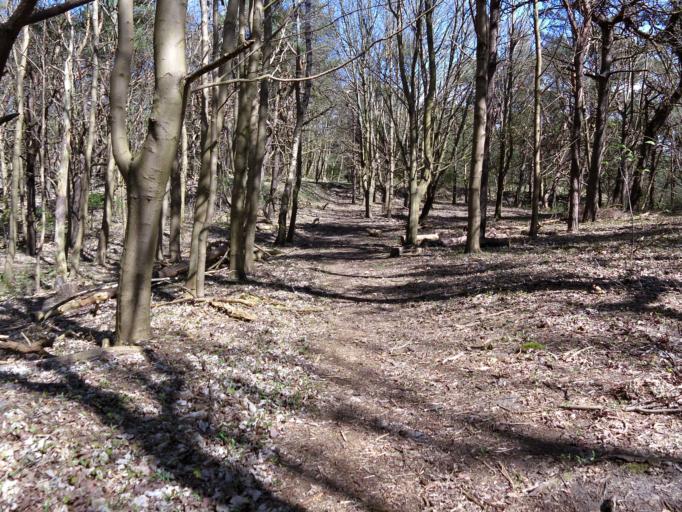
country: DE
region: Mecklenburg-Vorpommern
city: Hiddensee
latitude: 54.5924
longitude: 13.1086
